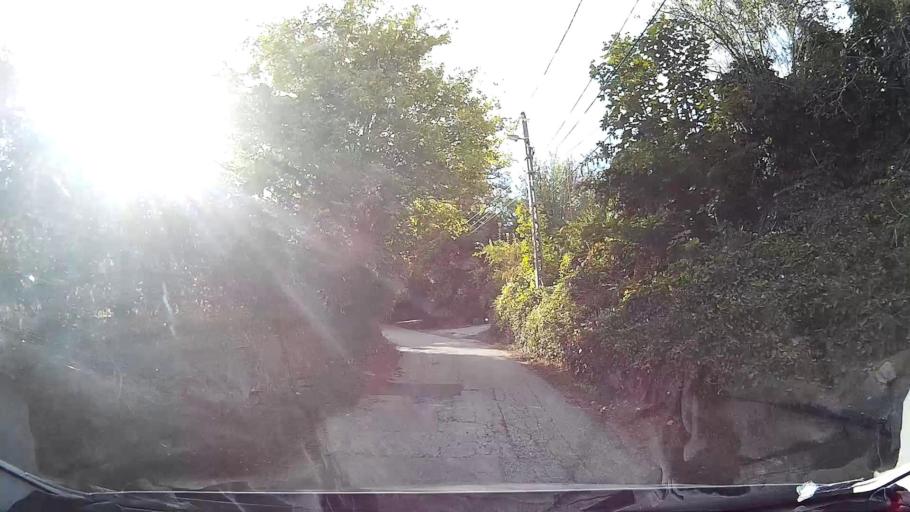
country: HU
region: Pest
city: Nagykovacsi
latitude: 47.6508
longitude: 19.0172
